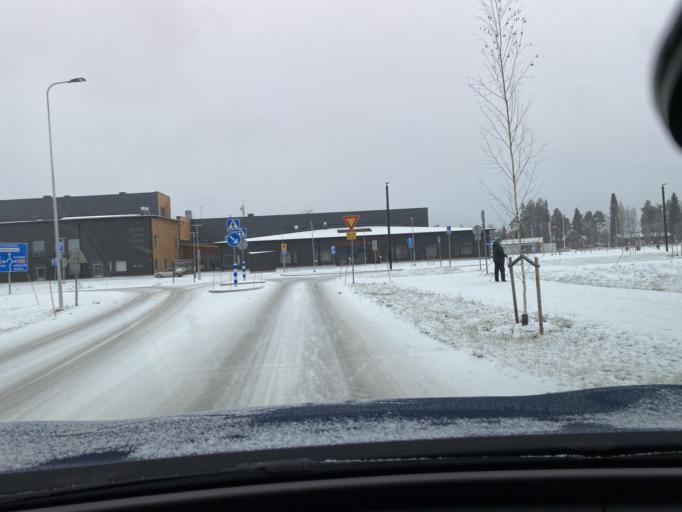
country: FI
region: Northern Ostrobothnia
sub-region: Oulunkaari
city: Pudasjaervi
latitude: 65.3582
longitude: 26.9873
